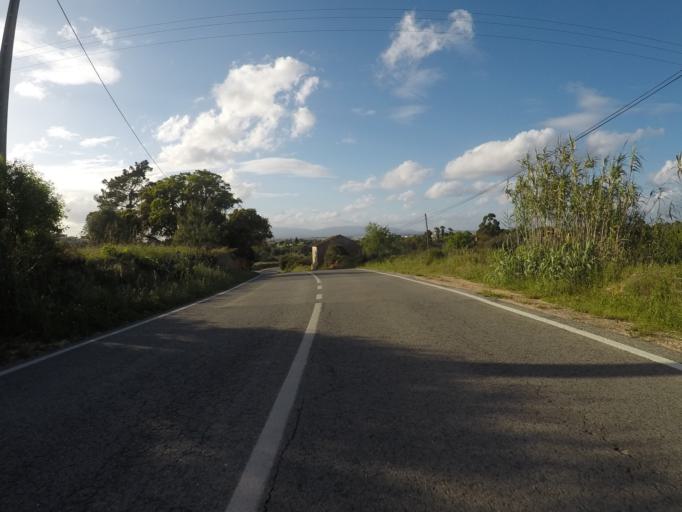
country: PT
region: Faro
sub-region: Lagoa
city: Carvoeiro
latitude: 37.1038
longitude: -8.4446
